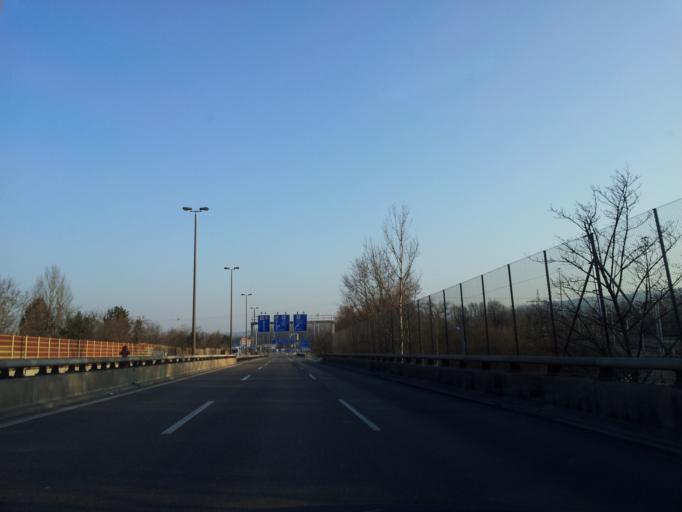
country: DE
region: Baden-Wuerttemberg
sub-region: Freiburg Region
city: Weil am Rhein
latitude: 47.5901
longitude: 7.6032
